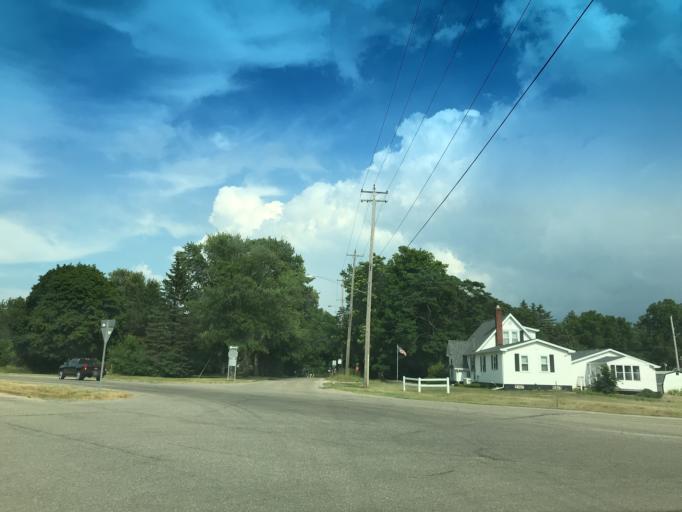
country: US
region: Michigan
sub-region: Eaton County
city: Waverly
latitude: 42.6976
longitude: -84.6295
